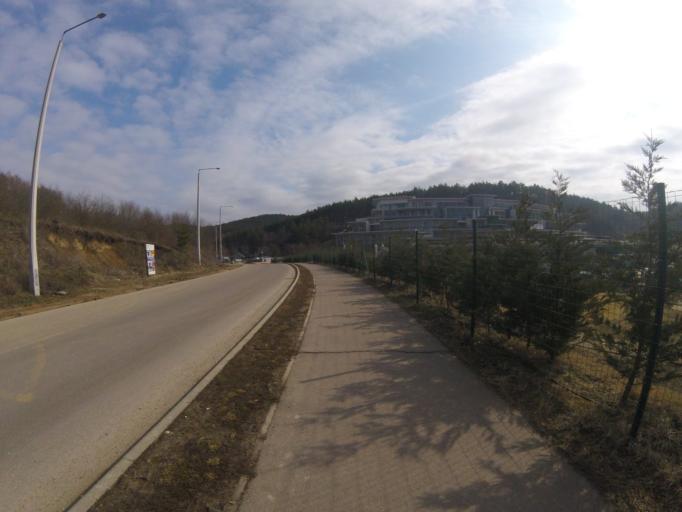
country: HU
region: Heves
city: Egerszalok
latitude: 47.8546
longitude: 20.3334
